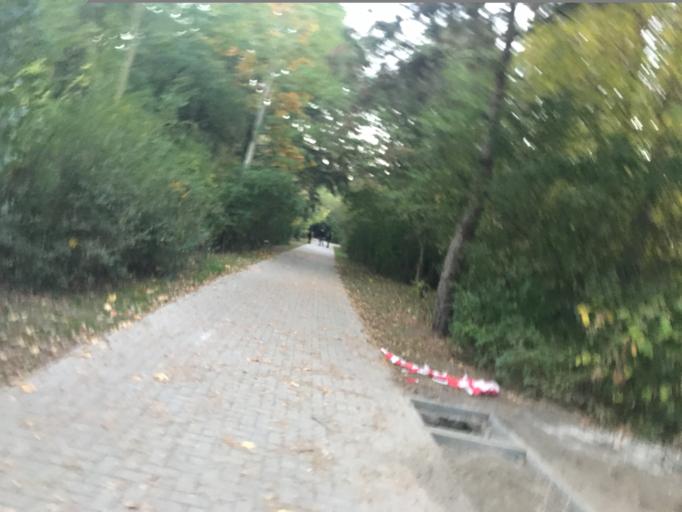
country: DE
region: Berlin
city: Britz
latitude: 52.4393
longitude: 13.4474
